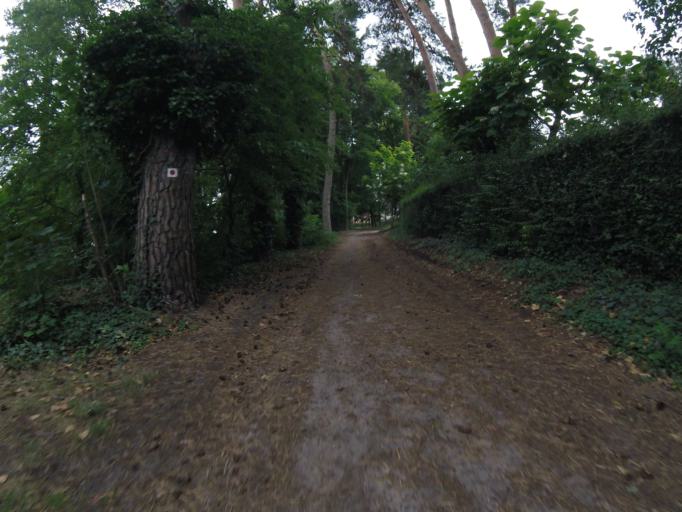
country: DE
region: Brandenburg
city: Bestensee
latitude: 52.2913
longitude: 13.7108
